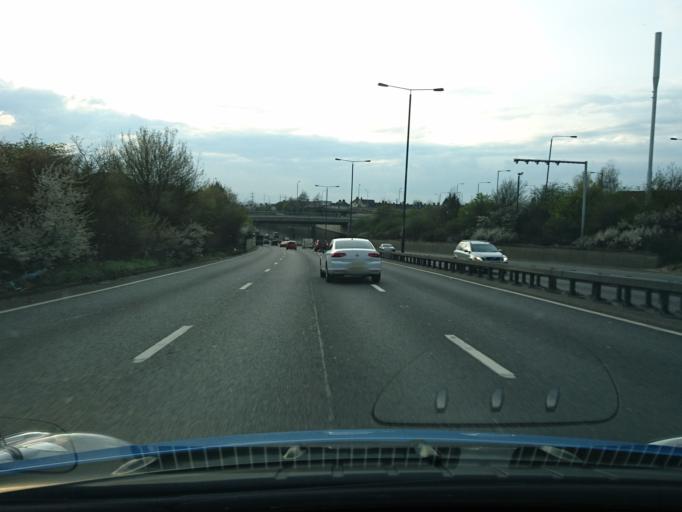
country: GB
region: England
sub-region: Greater London
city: Walthamstow
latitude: 51.5995
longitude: 0.0005
